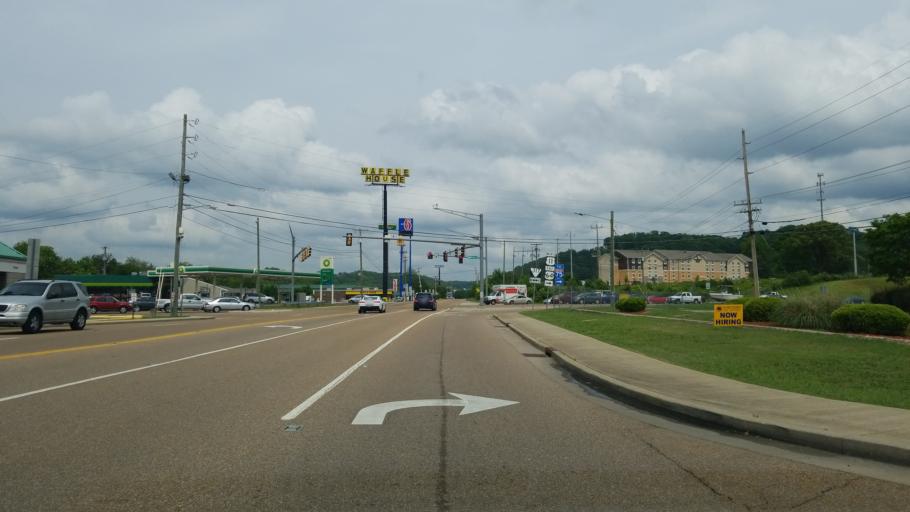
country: US
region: Tennessee
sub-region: Hamilton County
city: Harrison
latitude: 35.0602
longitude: -85.1350
